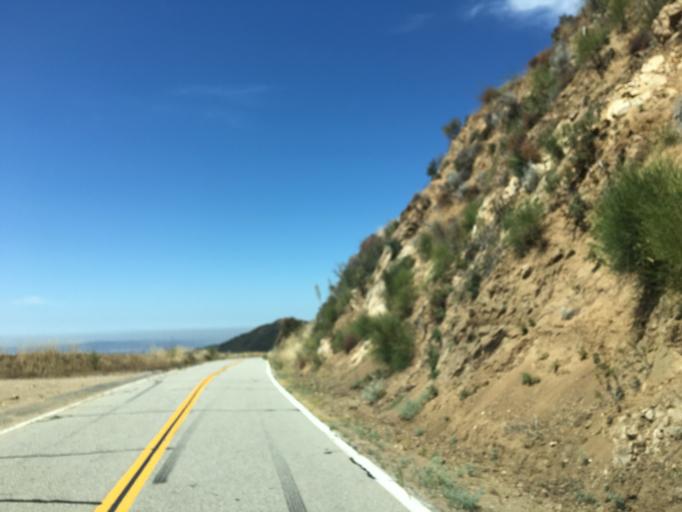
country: US
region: California
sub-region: Los Angeles County
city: Glendora
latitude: 34.2038
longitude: -117.8206
